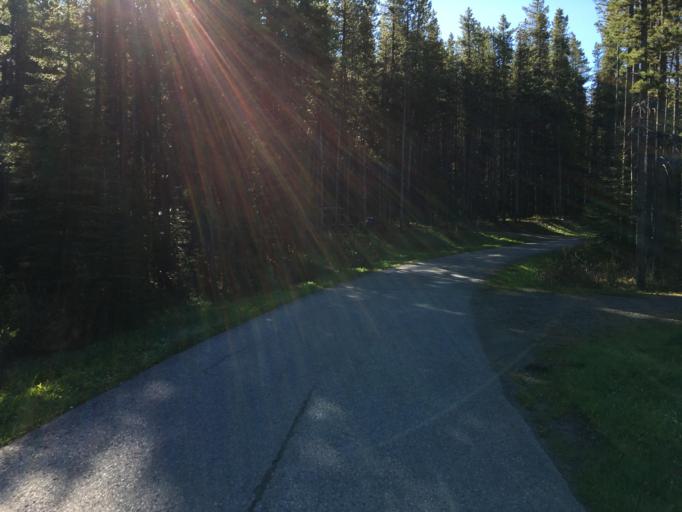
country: CA
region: Alberta
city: Canmore
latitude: 50.6350
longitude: -115.0975
